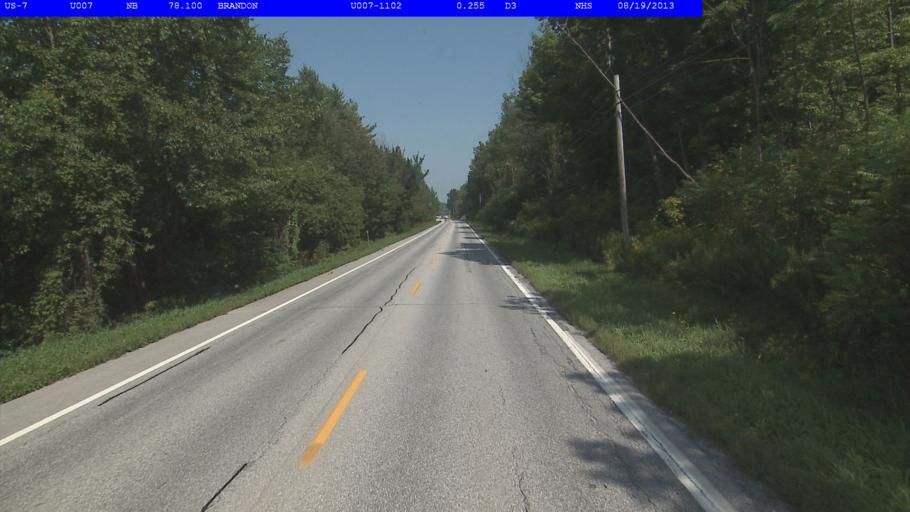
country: US
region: Vermont
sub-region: Rutland County
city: Brandon
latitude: 43.7580
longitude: -73.0488
